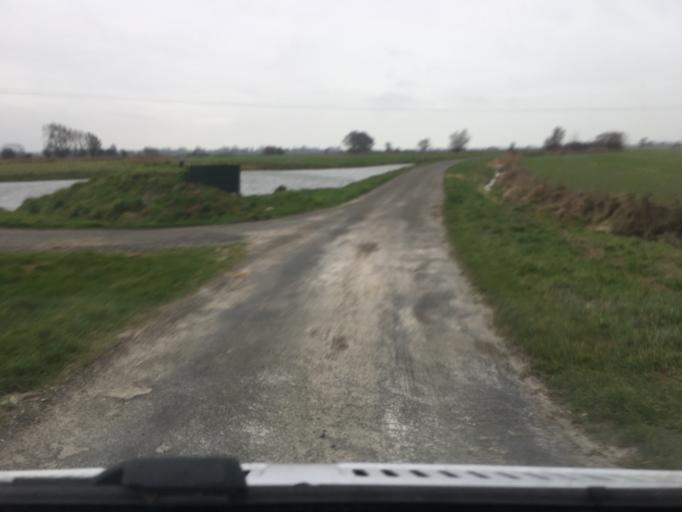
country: FR
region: Picardie
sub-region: Departement de la Somme
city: Pende
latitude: 50.1826
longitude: 1.5478
